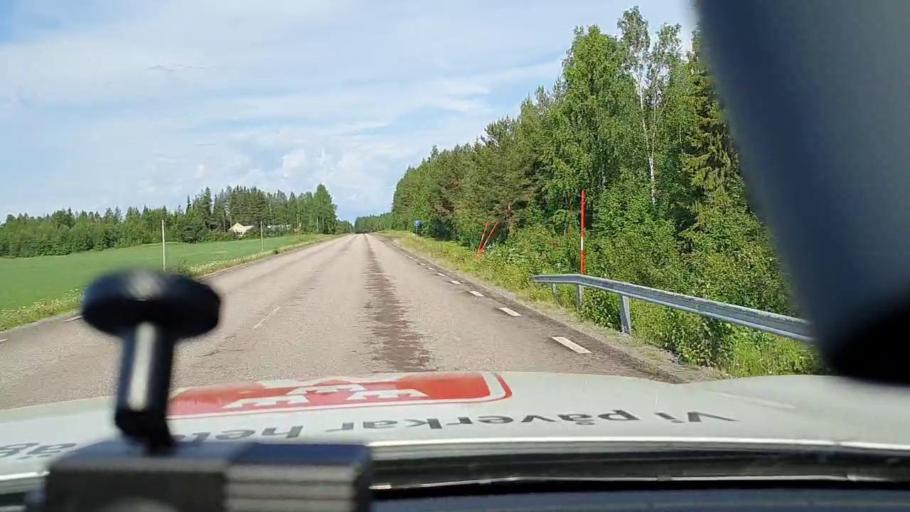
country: SE
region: Norrbotten
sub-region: Alvsbyns Kommun
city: AElvsbyn
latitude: 66.0186
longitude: 21.1458
